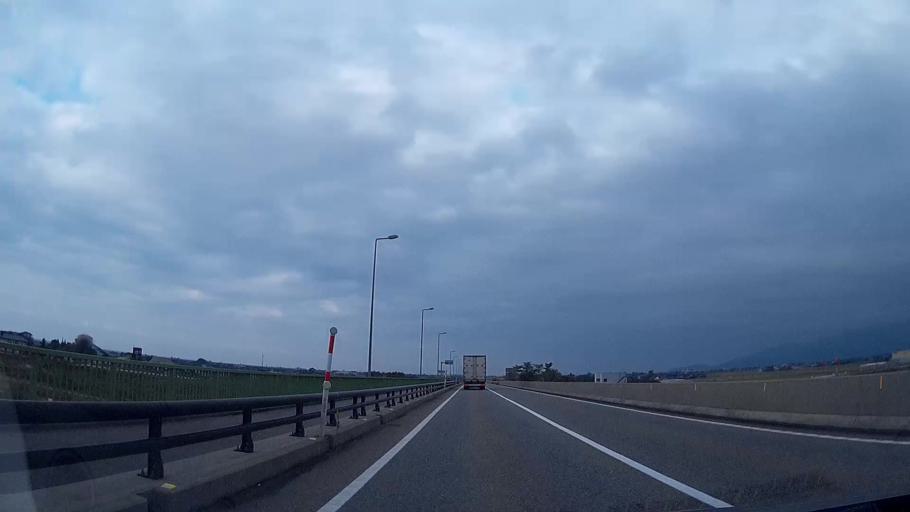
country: JP
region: Toyama
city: Nyuzen
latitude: 36.9062
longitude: 137.4517
